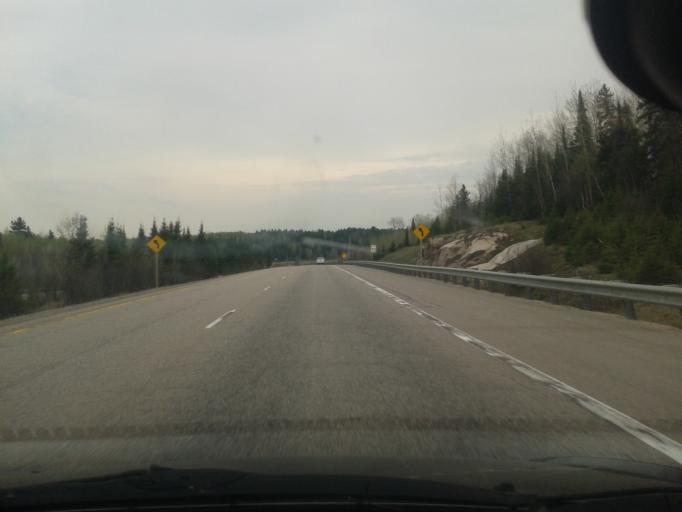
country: CA
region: Ontario
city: Powassan
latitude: 46.1927
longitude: -79.3582
